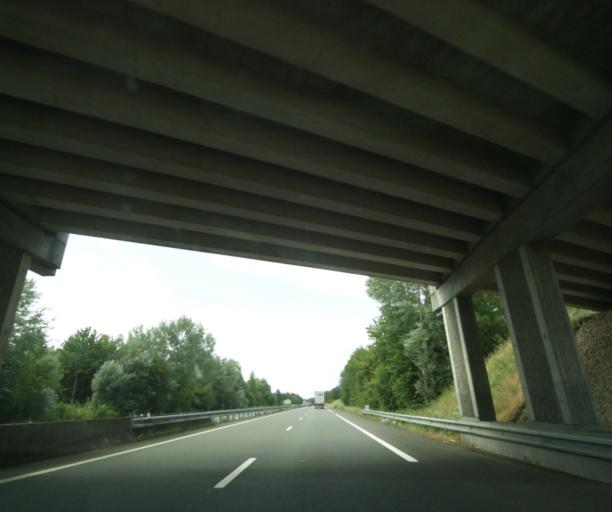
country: FR
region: Pays de la Loire
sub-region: Departement de Maine-et-Loire
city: Brion
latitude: 47.4611
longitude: -0.1830
